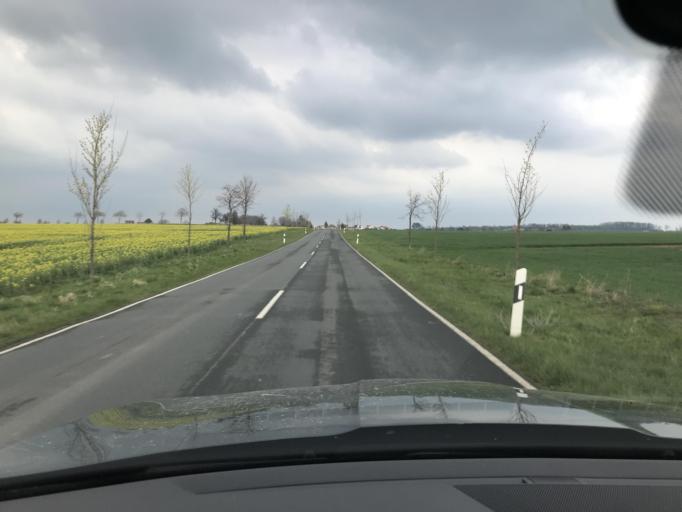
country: DE
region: Saxony-Anhalt
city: Ballenstedt
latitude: 51.7524
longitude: 11.2391
